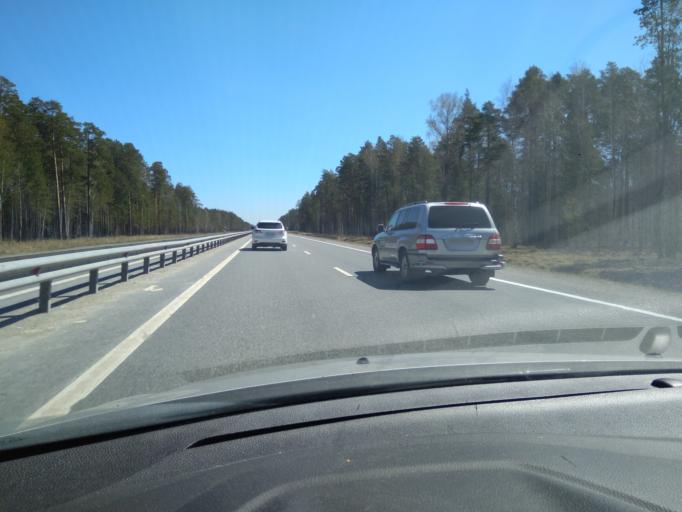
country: RU
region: Sverdlovsk
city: Lugovskoy
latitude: 57.0846
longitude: 64.4599
